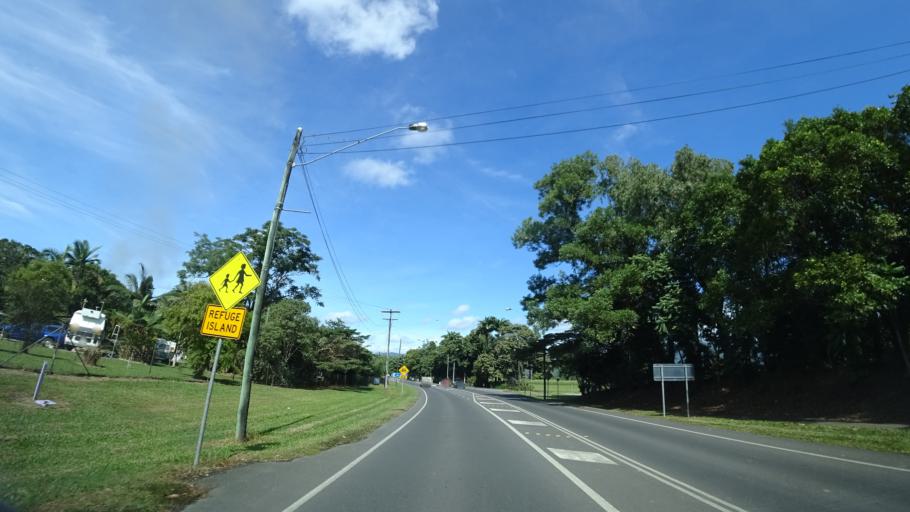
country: AU
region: Queensland
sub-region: Cairns
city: Port Douglas
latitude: -16.4540
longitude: 145.3715
